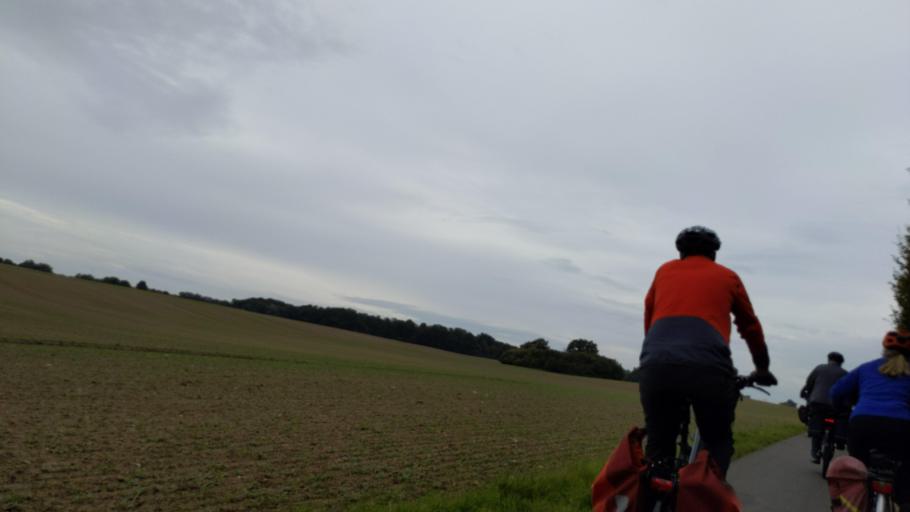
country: DE
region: Mecklenburg-Vorpommern
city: Schlagsdorf
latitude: 53.7464
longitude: 10.8278
